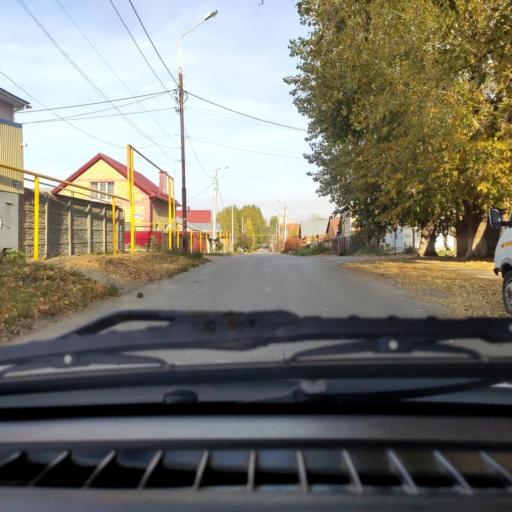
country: RU
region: Samara
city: Tol'yatti
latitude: 53.5244
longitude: 49.4050
